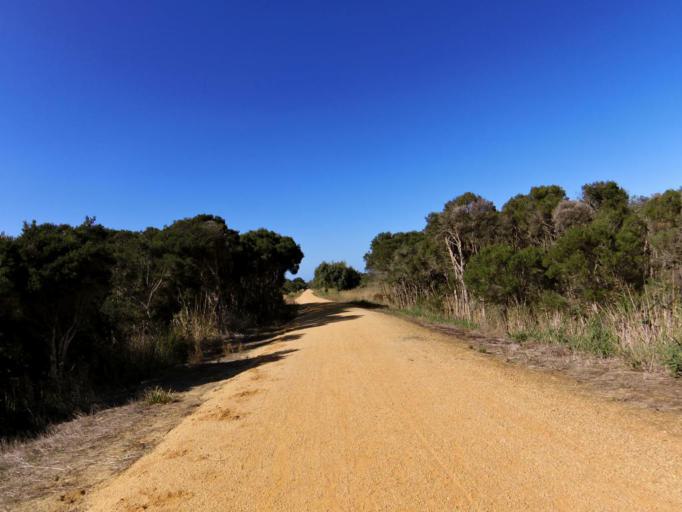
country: AU
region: Victoria
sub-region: Bass Coast
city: North Wonthaggi
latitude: -38.5820
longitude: 145.5535
